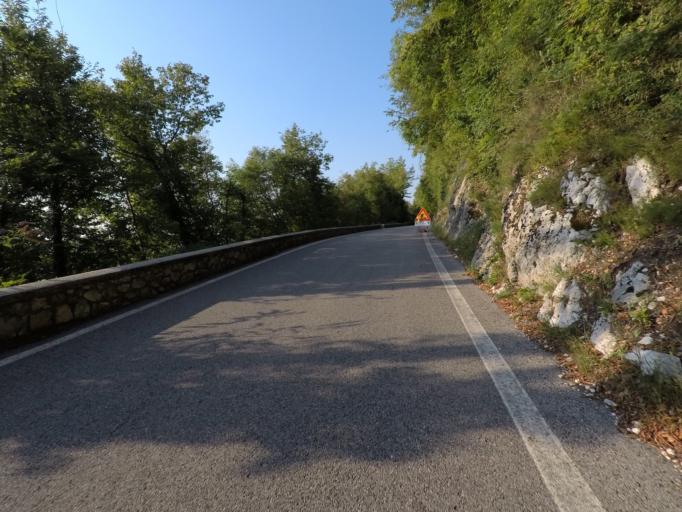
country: IT
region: Friuli Venezia Giulia
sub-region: Provincia di Udine
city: Osoppo
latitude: 46.2457
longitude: 13.0363
